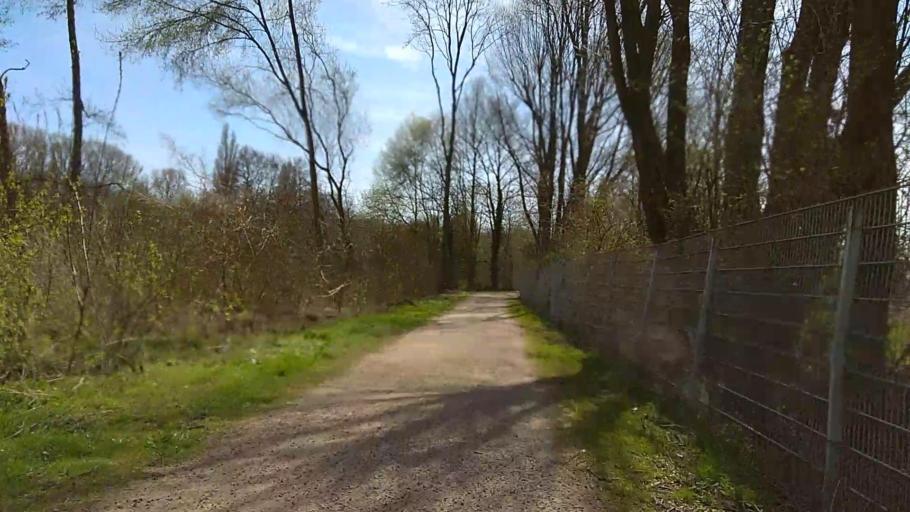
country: DE
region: North Rhine-Westphalia
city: Herten
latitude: 51.5629
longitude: 7.1000
